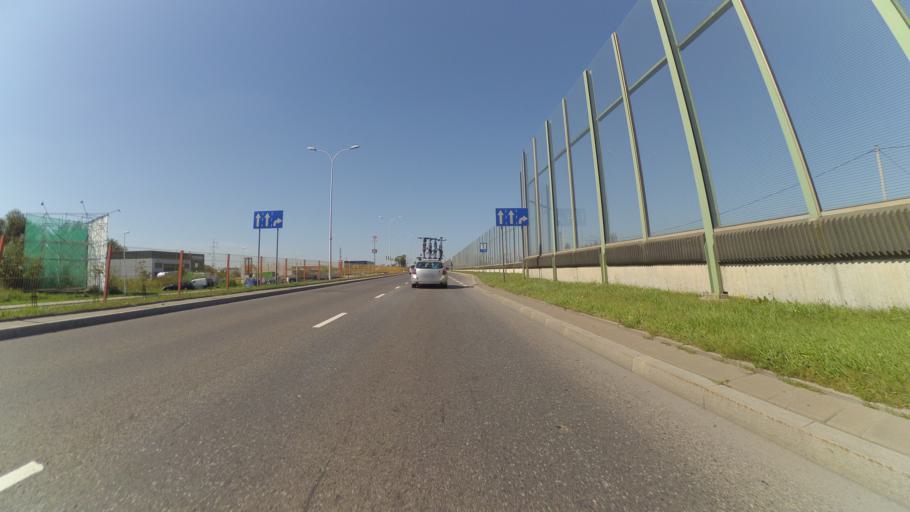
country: PL
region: Podlasie
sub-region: Bialystok
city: Bialystok
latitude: 53.1595
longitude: 23.1216
